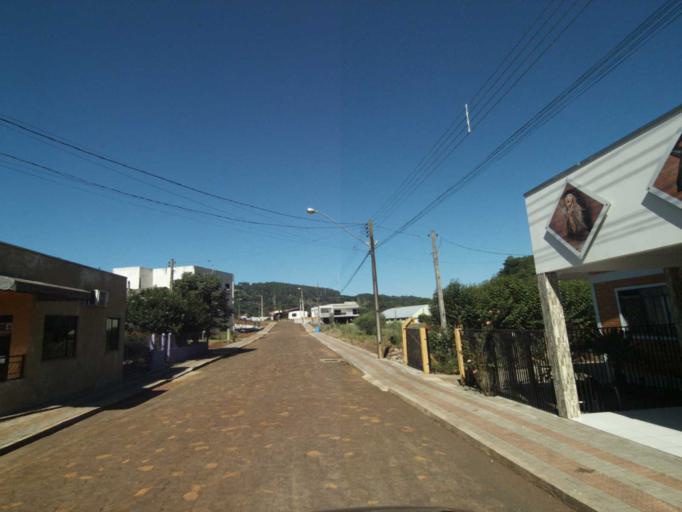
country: BR
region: Parana
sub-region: Francisco Beltrao
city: Francisco Beltrao
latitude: -26.1429
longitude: -53.3088
